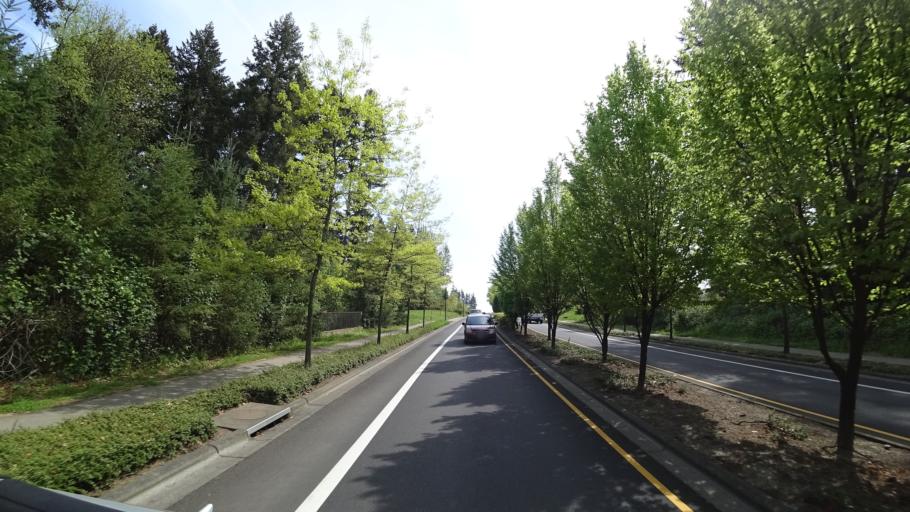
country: US
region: Oregon
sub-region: Washington County
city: Hillsboro
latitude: 45.5245
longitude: -122.9368
